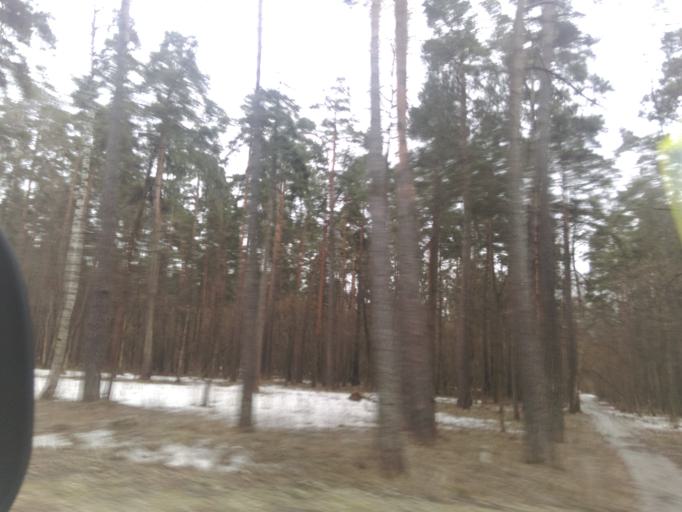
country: RU
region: Moscow
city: Rublevo
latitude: 55.7606
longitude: 37.3497
